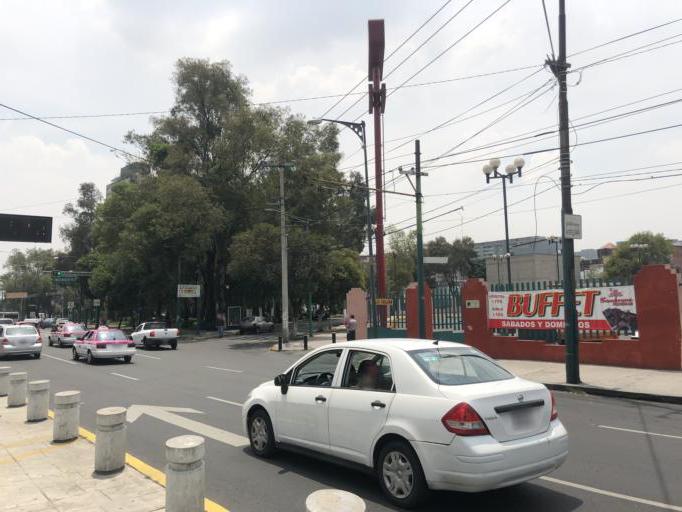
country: MX
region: Mexico City
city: Cuauhtemoc
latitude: 19.4542
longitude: -99.1305
